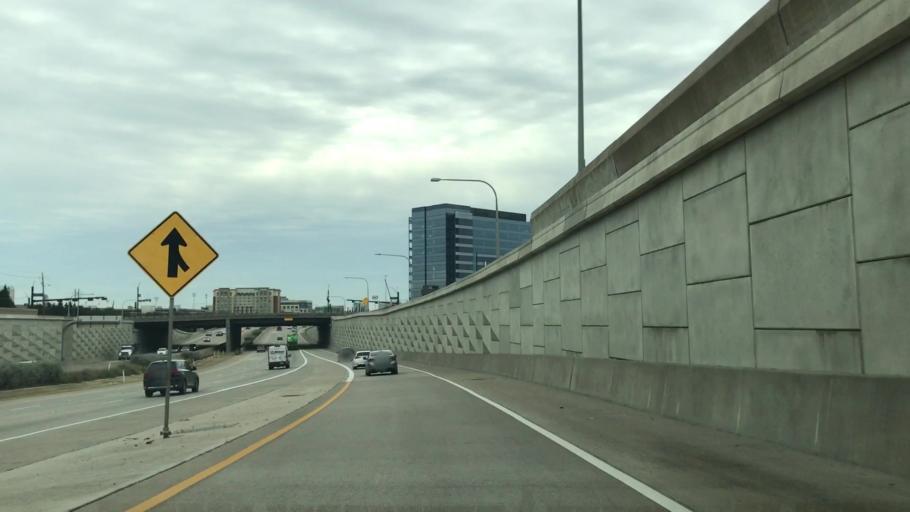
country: US
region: Texas
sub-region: Collin County
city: Frisco
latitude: 33.1090
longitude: -96.8238
